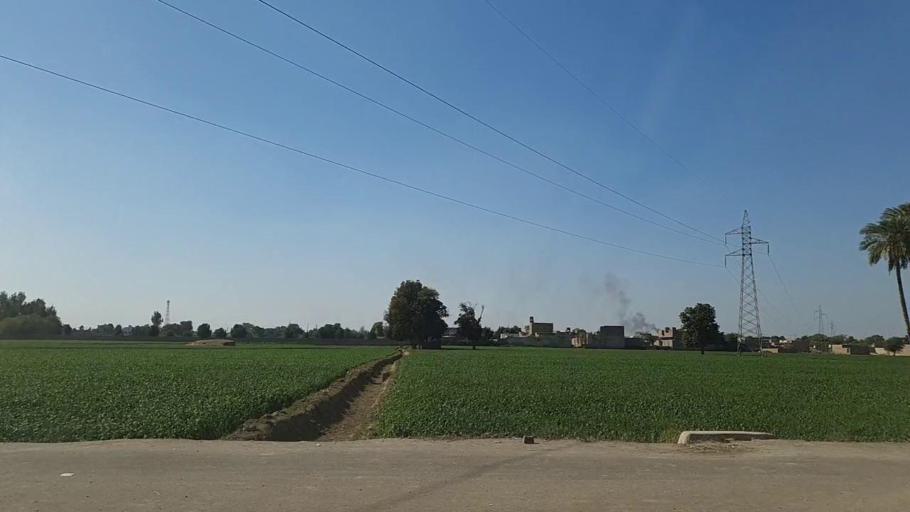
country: PK
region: Sindh
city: Nawabshah
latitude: 26.2547
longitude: 68.4362
